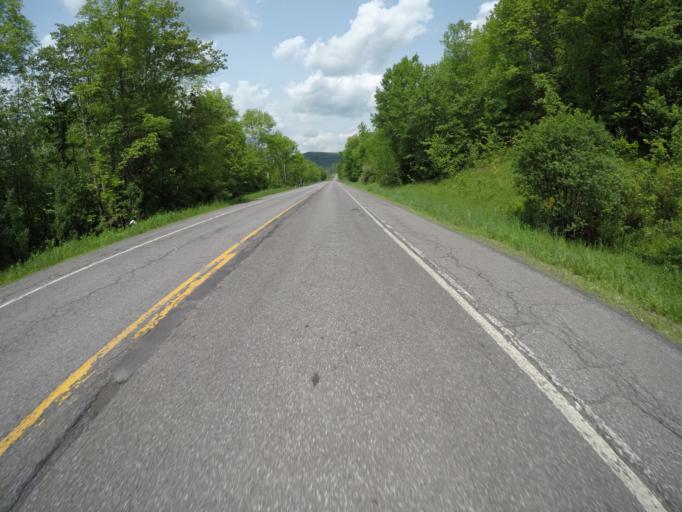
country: US
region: New York
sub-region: Delaware County
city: Stamford
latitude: 42.2140
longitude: -74.5929
